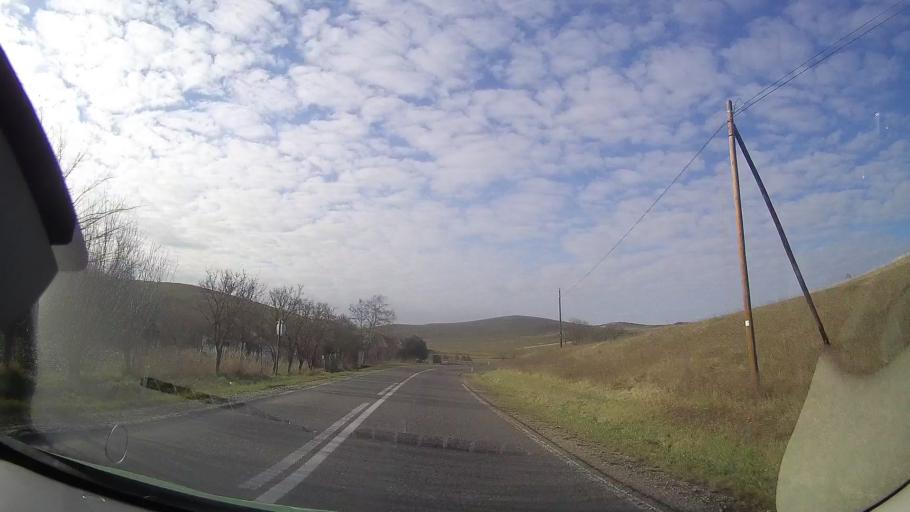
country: RO
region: Cluj
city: Jucu Herghelia
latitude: 46.8117
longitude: 23.8187
